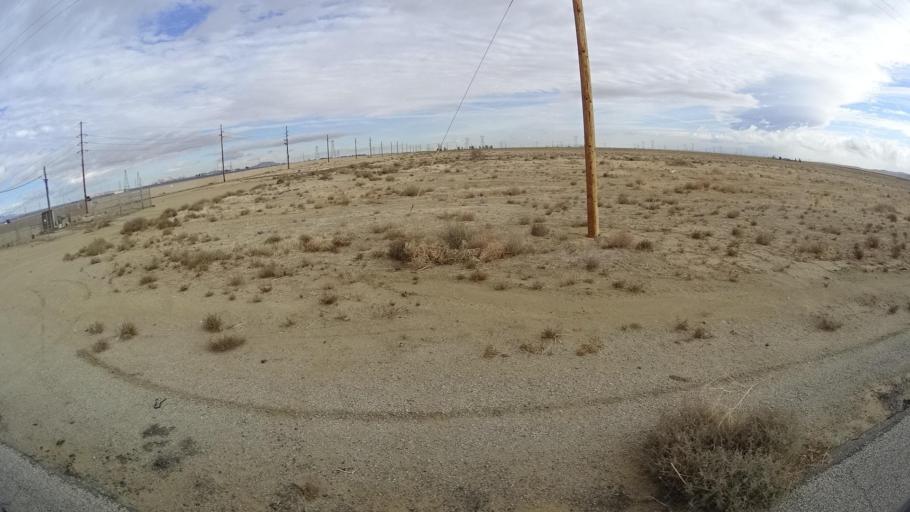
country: US
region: California
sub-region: Los Angeles County
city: Green Valley
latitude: 34.8256
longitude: -118.4316
